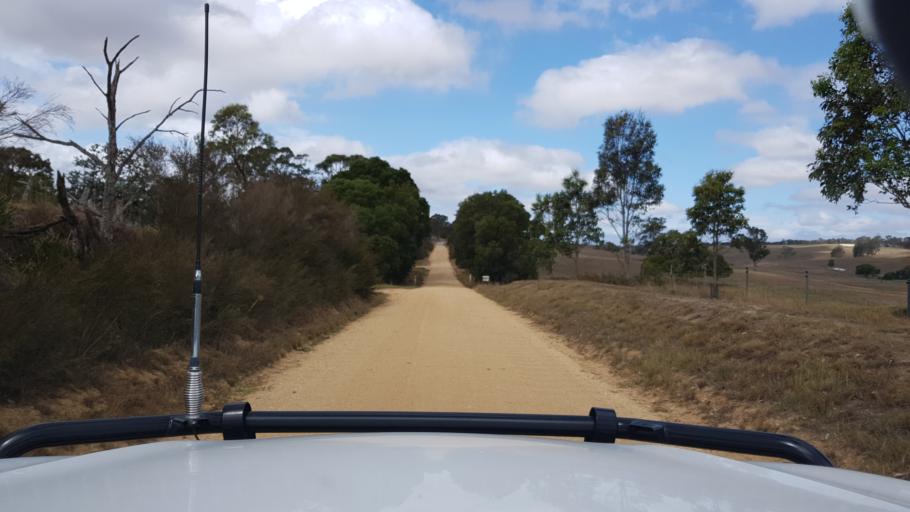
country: AU
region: Victoria
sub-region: East Gippsland
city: Bairnsdale
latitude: -37.7854
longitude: 147.5554
